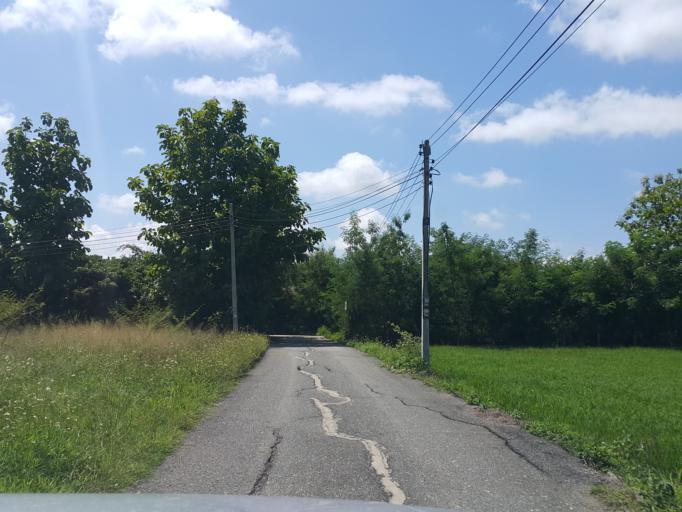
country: TH
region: Chiang Mai
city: San Kamphaeng
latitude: 18.7170
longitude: 99.1065
